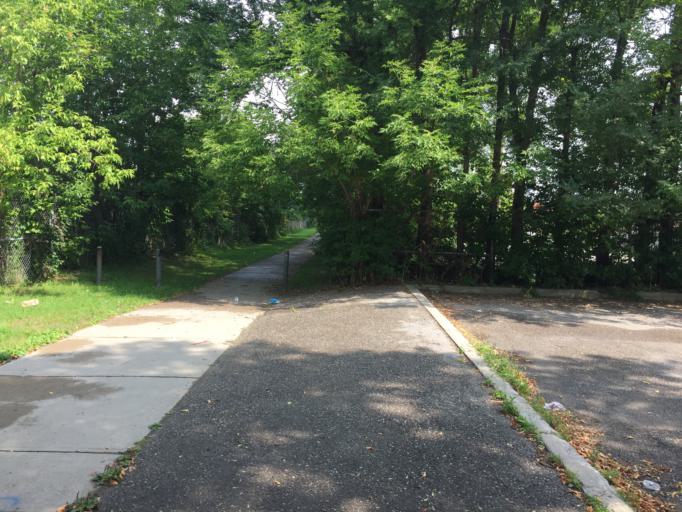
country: CA
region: Ontario
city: Oshawa
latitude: 43.8874
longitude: -78.8555
